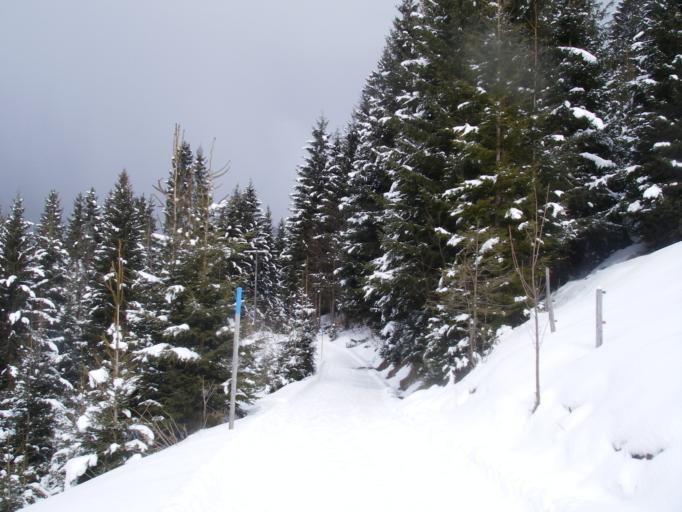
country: AT
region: Vorarlberg
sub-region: Politischer Bezirk Bregenz
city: Mittelberg
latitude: 47.3429
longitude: 10.1741
